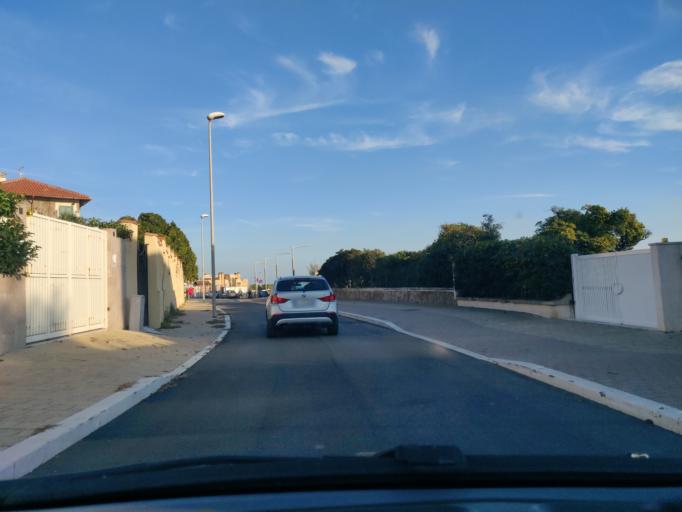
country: IT
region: Latium
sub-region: Citta metropolitana di Roma Capitale
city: Santa Marinella
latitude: 42.0298
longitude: 11.8358
